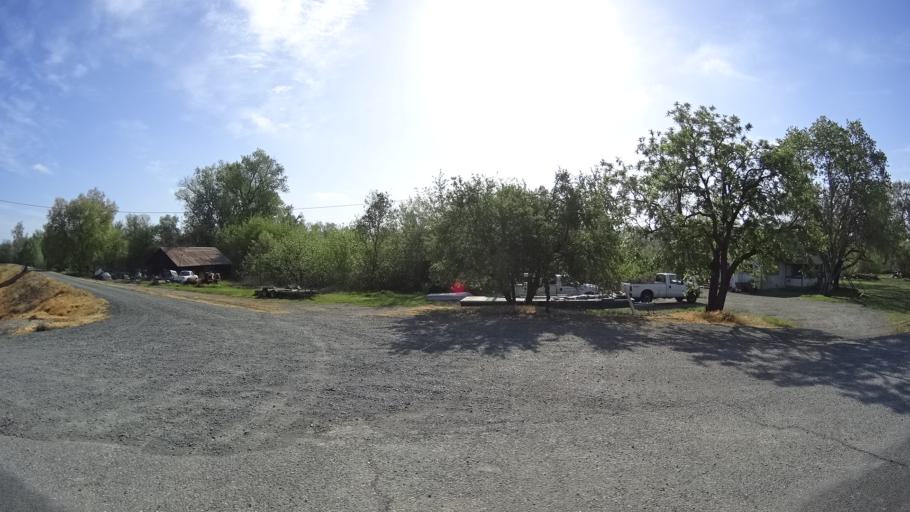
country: US
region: California
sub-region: Glenn County
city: Hamilton City
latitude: 39.5846
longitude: -122.0076
